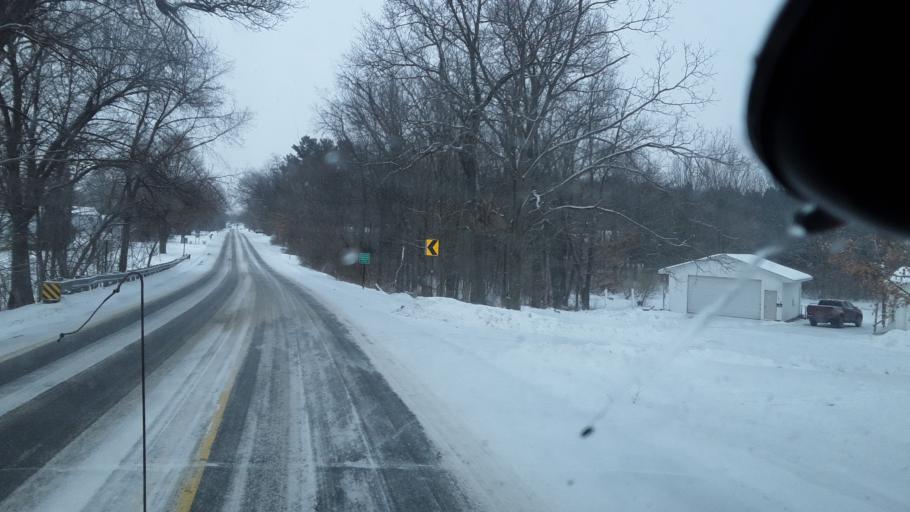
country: US
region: Michigan
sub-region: Ingham County
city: Mason
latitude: 42.5441
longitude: -84.3642
